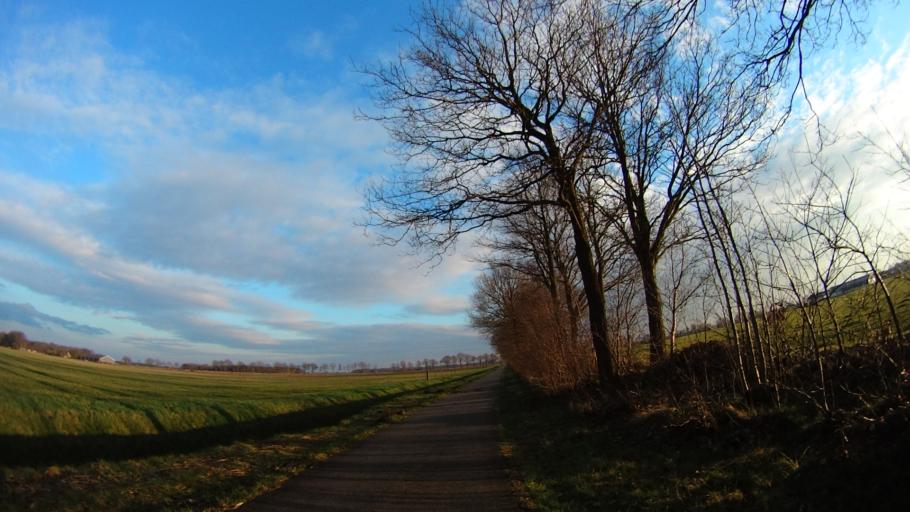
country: NL
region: Drenthe
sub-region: Gemeente Coevorden
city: Sleen
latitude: 52.7903
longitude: 6.7788
